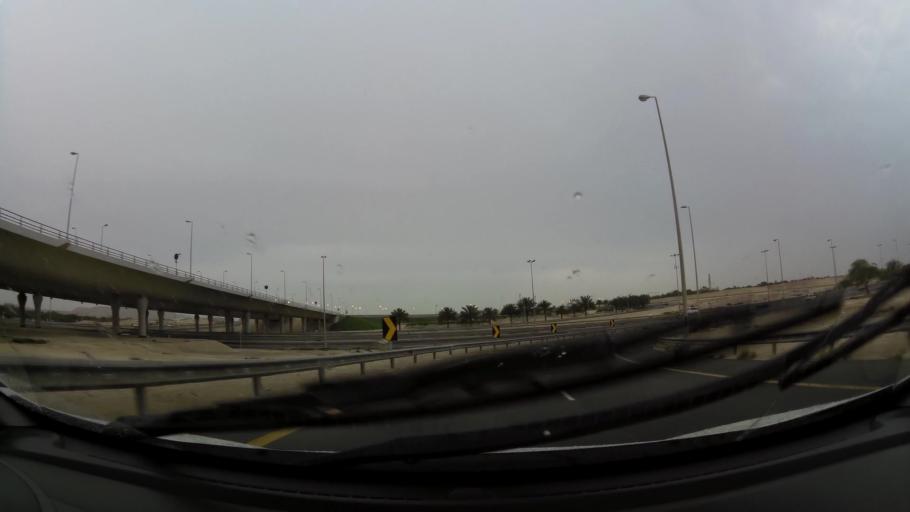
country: BH
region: Central Governorate
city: Dar Kulayb
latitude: 26.0602
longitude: 50.5172
